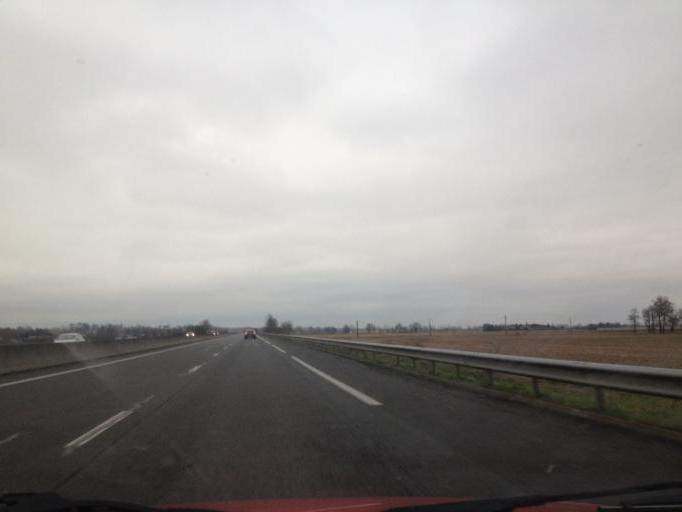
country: FR
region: Auvergne
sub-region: Departement de l'Allier
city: Toulon-sur-Allier
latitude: 46.5214
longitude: 3.3510
